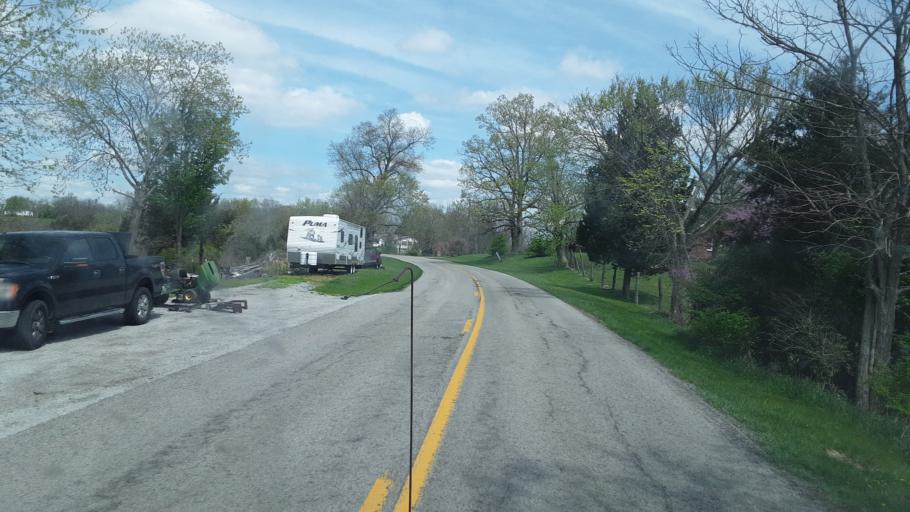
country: US
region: Kentucky
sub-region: Grant County
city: Dry Ridge
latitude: 38.6511
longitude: -84.7038
